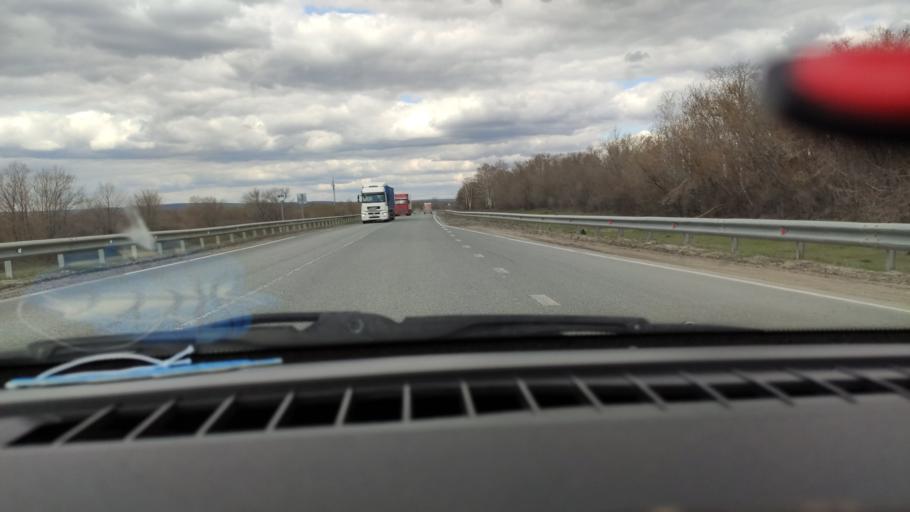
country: RU
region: Saratov
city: Tersa
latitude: 52.0895
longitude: 47.5465
